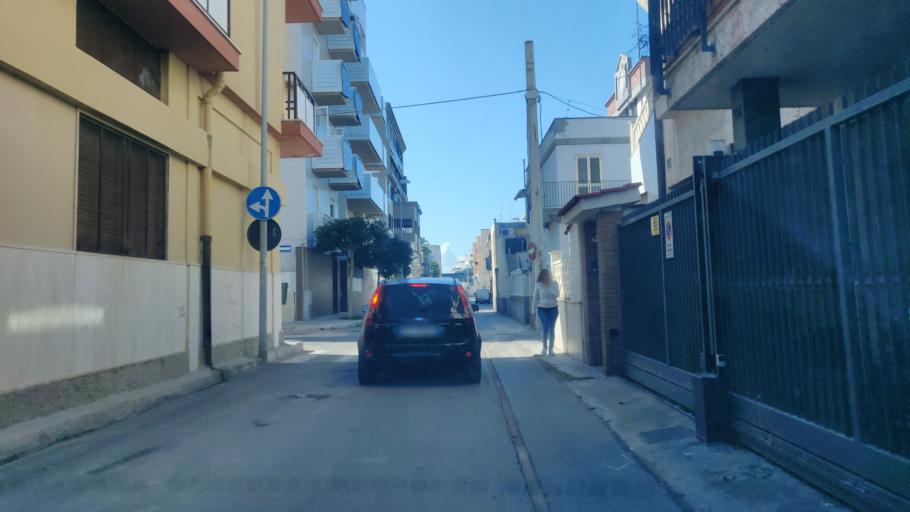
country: IT
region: Apulia
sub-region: Provincia di Bari
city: San Paolo
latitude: 41.1389
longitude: 16.8137
